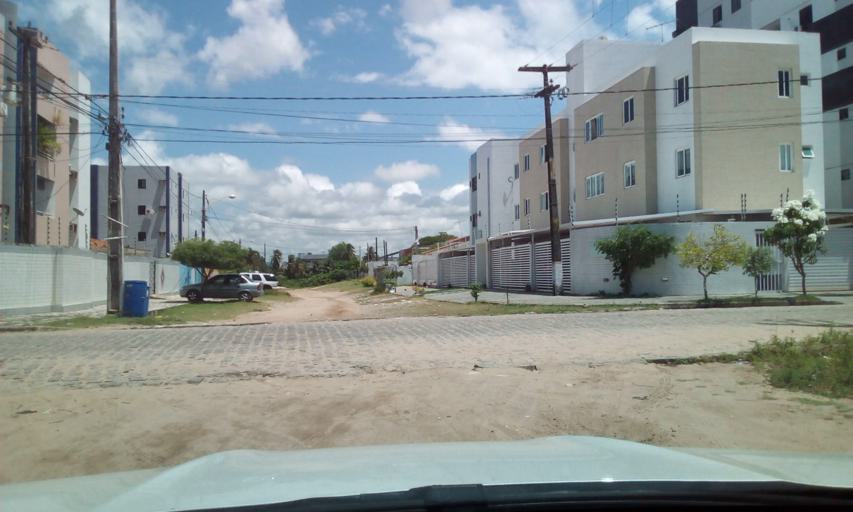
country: BR
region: Paraiba
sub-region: Joao Pessoa
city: Joao Pessoa
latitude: -7.0719
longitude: -34.8453
